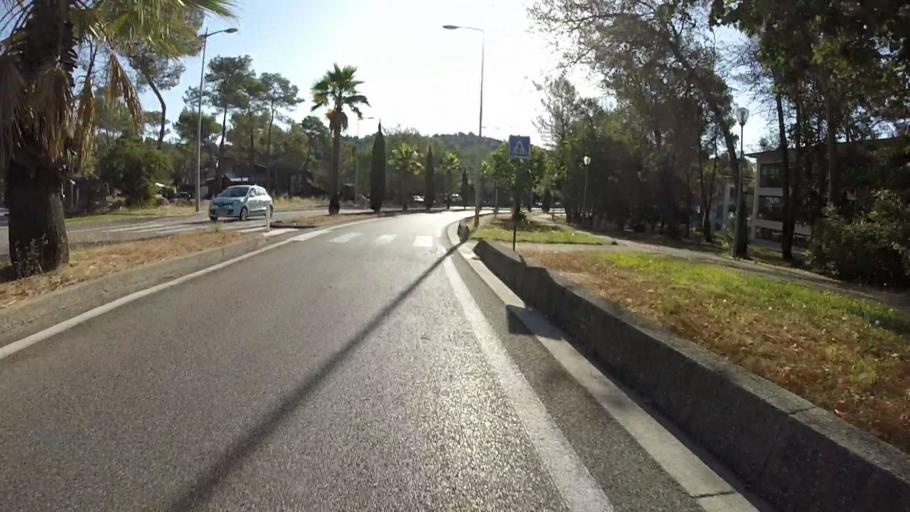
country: FR
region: Provence-Alpes-Cote d'Azur
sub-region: Departement des Alpes-Maritimes
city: Mougins
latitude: 43.6123
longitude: 7.0143
